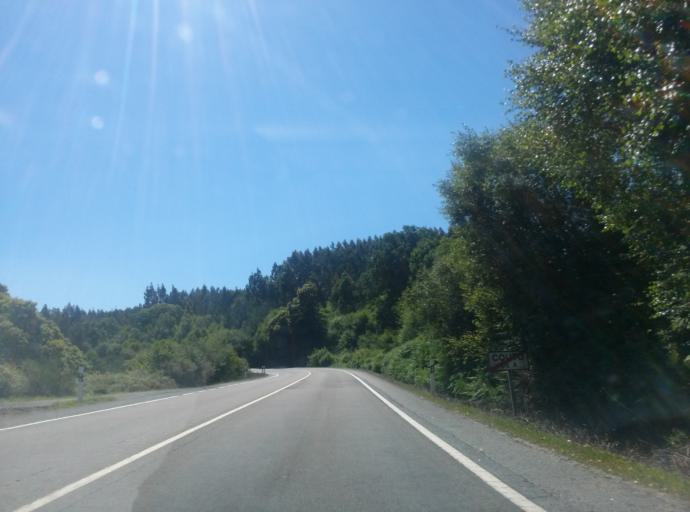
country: ES
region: Galicia
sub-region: Provincia de Lugo
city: Castro de Rei
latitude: 43.1618
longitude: -7.3807
